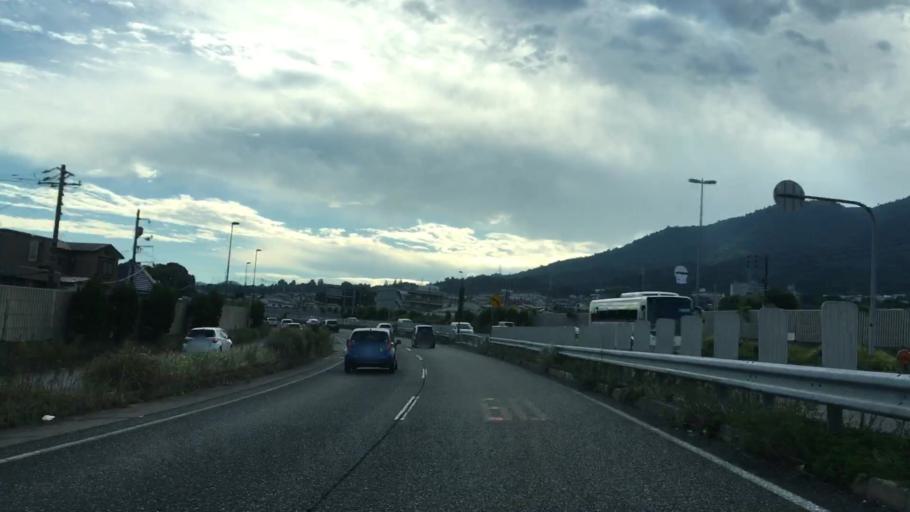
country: JP
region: Hiroshima
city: Hatsukaichi
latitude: 34.3822
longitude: 132.3518
